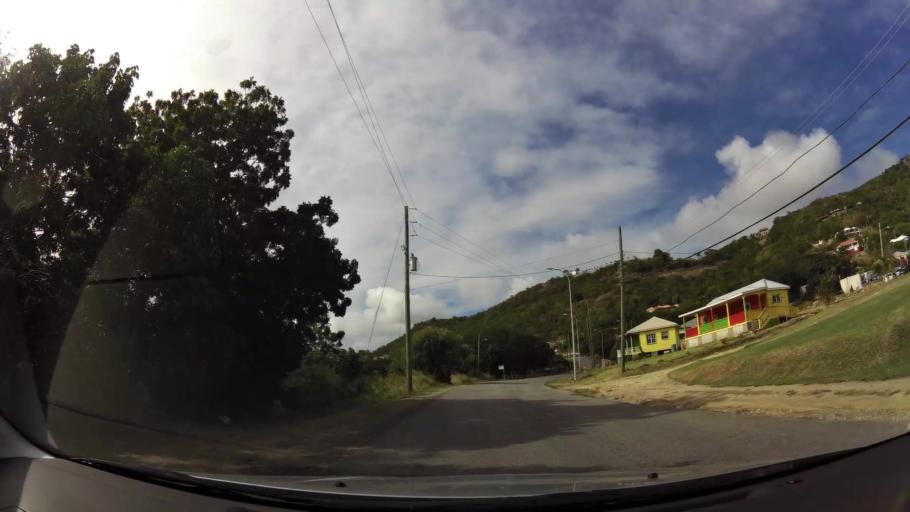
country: AG
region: Saint Paul
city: Falmouth
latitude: 17.0262
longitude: -61.7807
